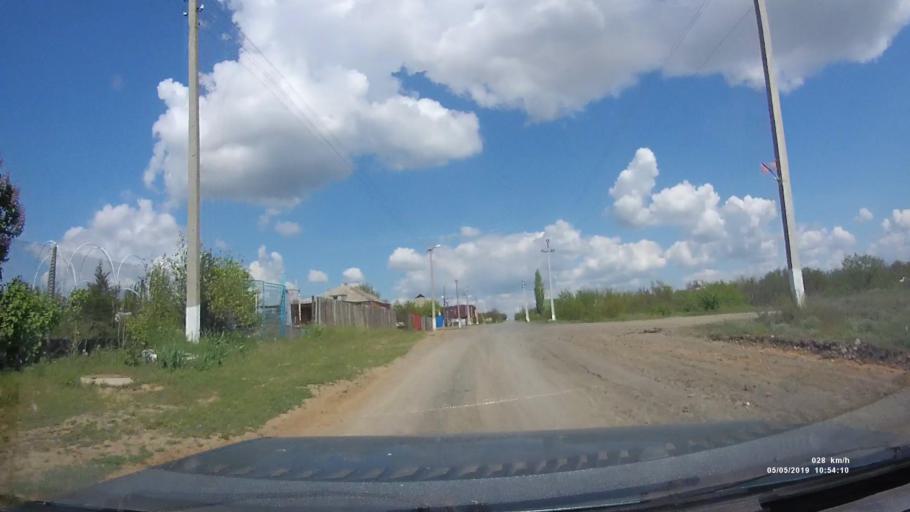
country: RU
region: Rostov
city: Ust'-Donetskiy
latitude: 47.6570
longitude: 40.8234
